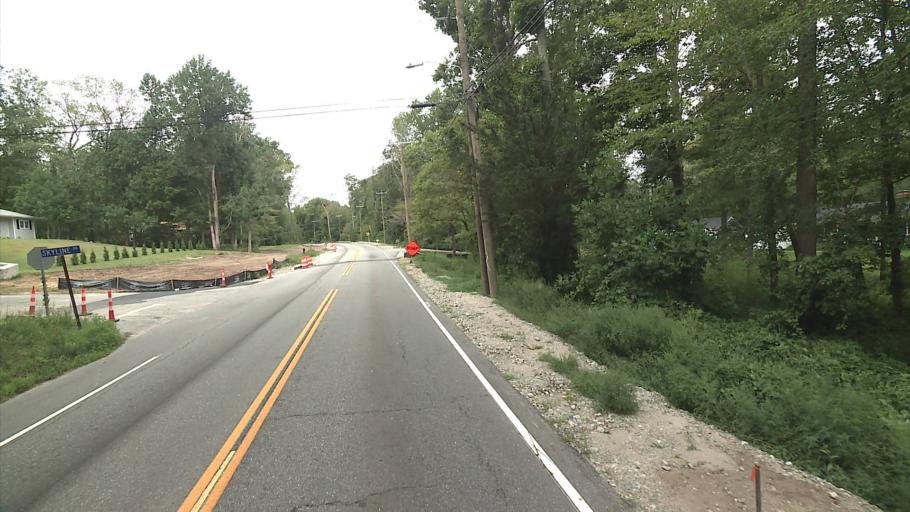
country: US
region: Connecticut
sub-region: New London County
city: Montville Center
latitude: 41.4517
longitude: -72.2364
